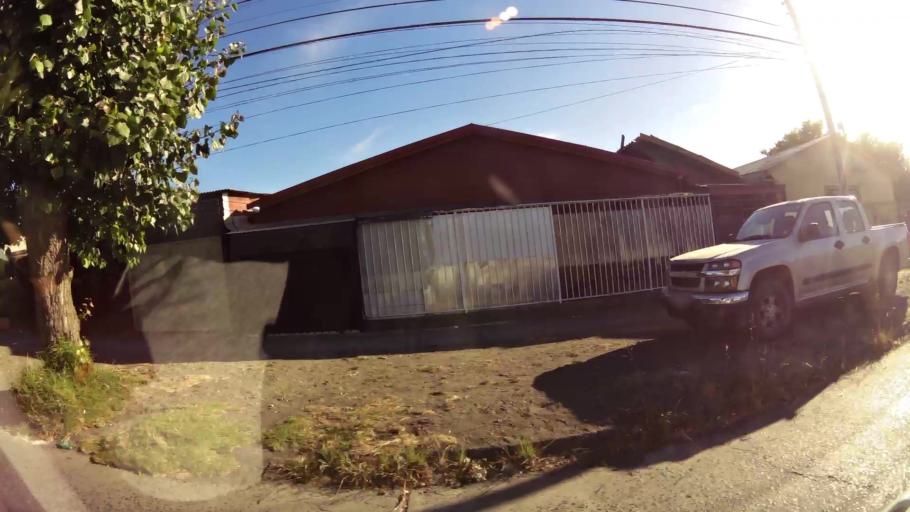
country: CL
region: Biobio
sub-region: Provincia de Concepcion
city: Concepcion
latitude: -36.8263
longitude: -73.1250
